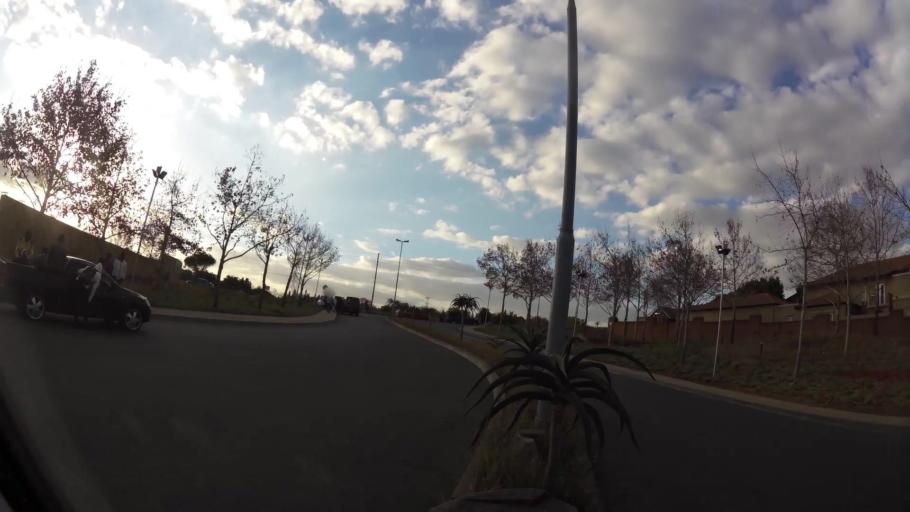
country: ZA
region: Gauteng
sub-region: City of Johannesburg Metropolitan Municipality
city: Diepsloot
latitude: -26.0046
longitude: 27.9780
